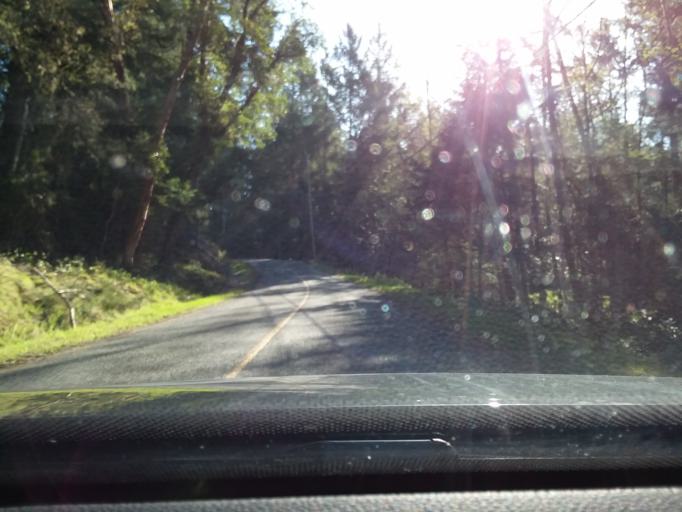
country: CA
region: British Columbia
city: North Cowichan
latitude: 48.9486
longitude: -123.5216
